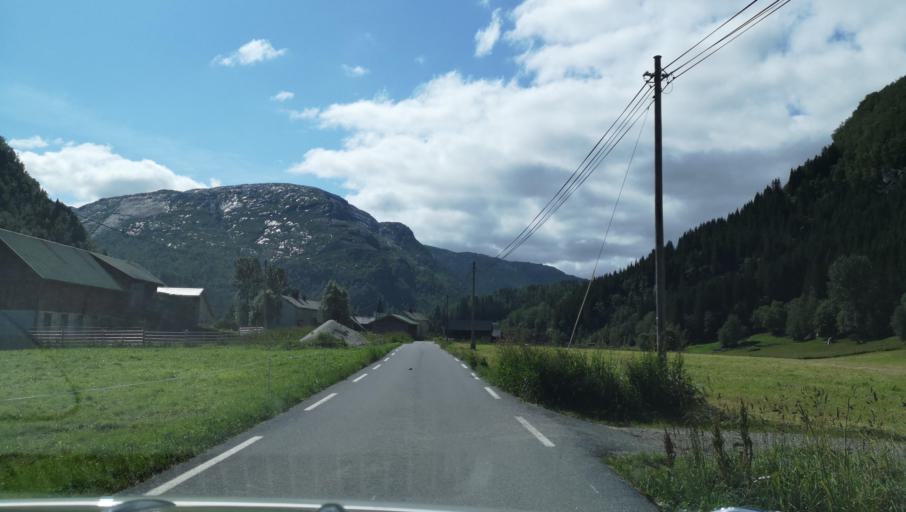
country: NO
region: Hordaland
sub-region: Modalen
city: Mo
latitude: 60.7858
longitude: 5.9639
